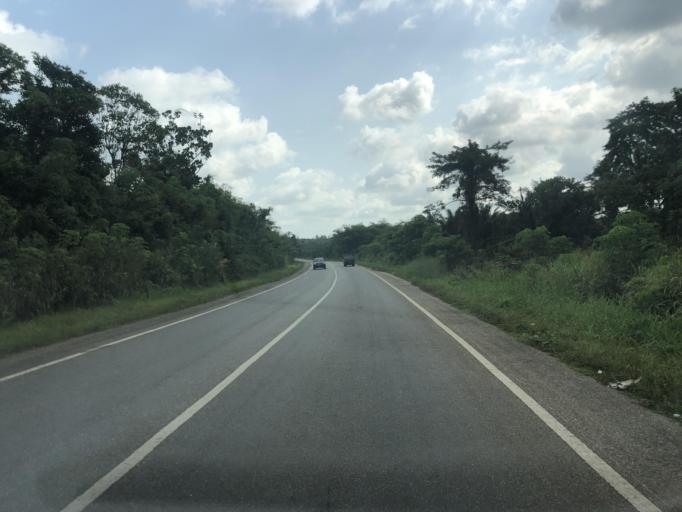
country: GH
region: Central
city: Cape Coast
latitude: 5.2243
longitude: -1.3242
